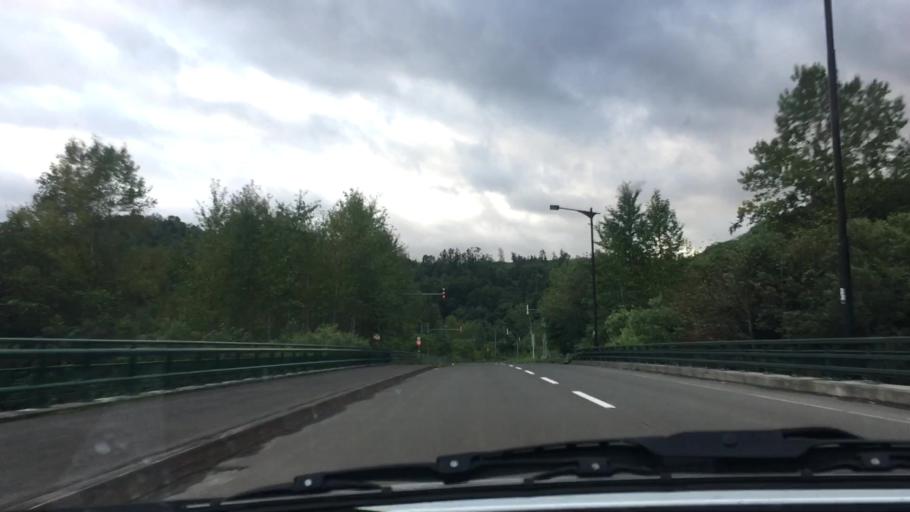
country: JP
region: Hokkaido
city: Shimo-furano
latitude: 42.9790
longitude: 142.3911
